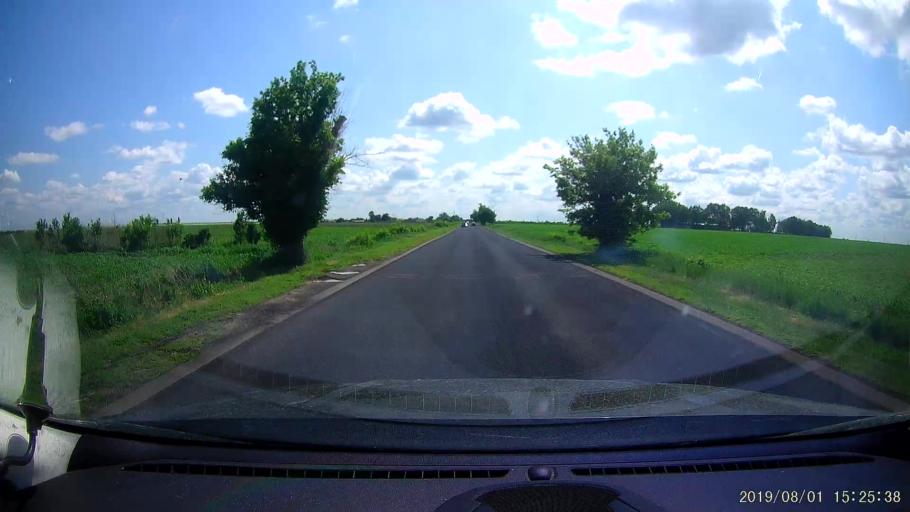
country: RO
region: Braila
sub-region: Comuna Viziru
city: Lanurile
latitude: 45.0195
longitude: 27.7324
